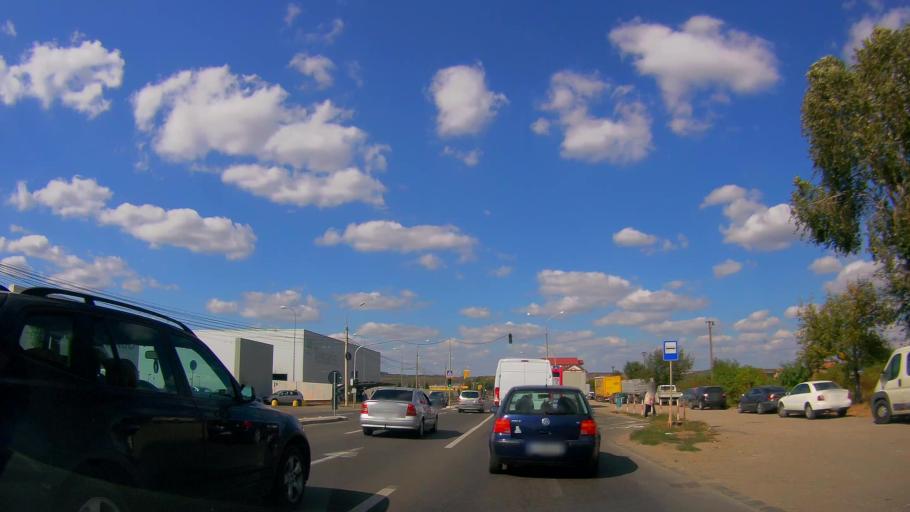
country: RO
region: Salaj
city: Zalau
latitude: 47.2123
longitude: 23.0435
